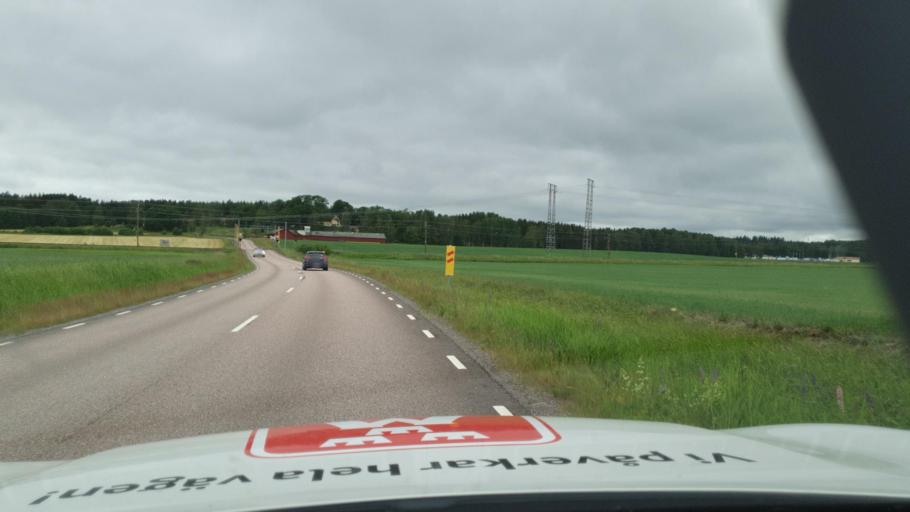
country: SE
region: Vaermland
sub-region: Karlstads Kommun
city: Edsvalla
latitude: 59.4190
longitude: 13.2138
